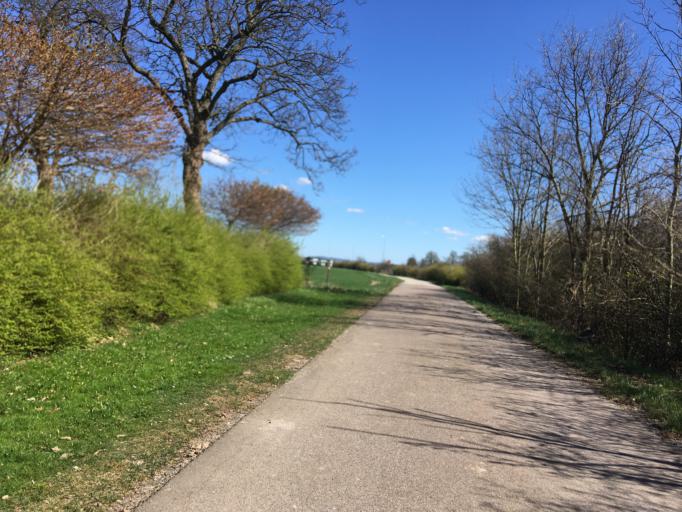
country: SE
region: Skane
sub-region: Staffanstorps Kommun
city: Hjaerup
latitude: 55.6812
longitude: 13.1682
